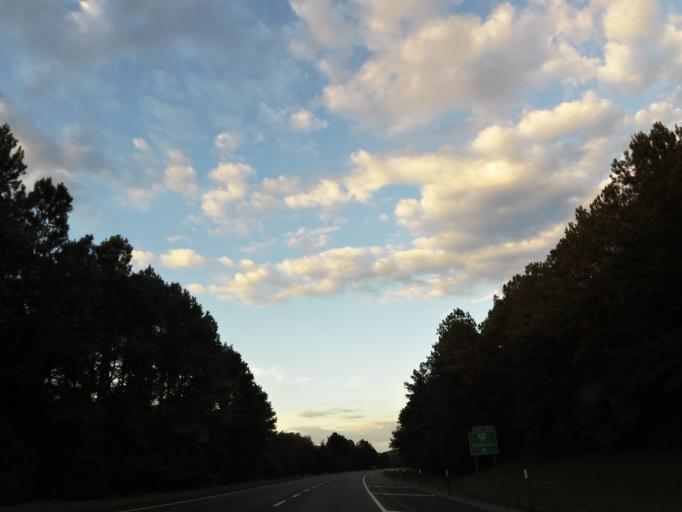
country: US
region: Tennessee
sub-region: Bradley County
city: Hopewell
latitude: 35.3219
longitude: -84.7896
